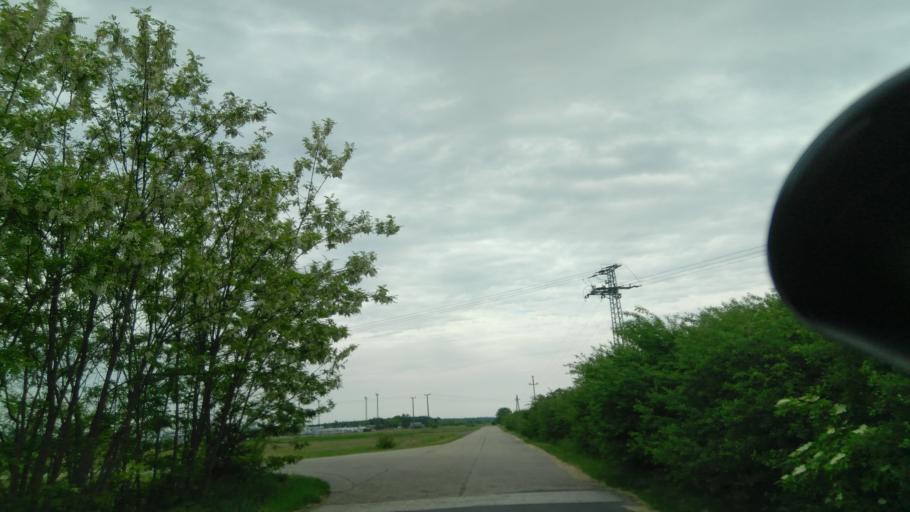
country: HU
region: Bekes
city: Fuzesgyarmat
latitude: 47.0871
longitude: 21.2078
